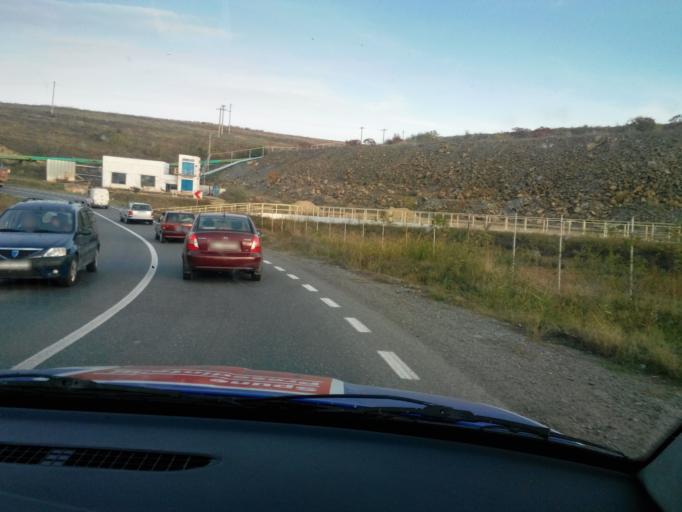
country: RO
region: Tulcea
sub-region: Comuna Somova
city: Mineri
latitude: 45.1661
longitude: 28.7324
